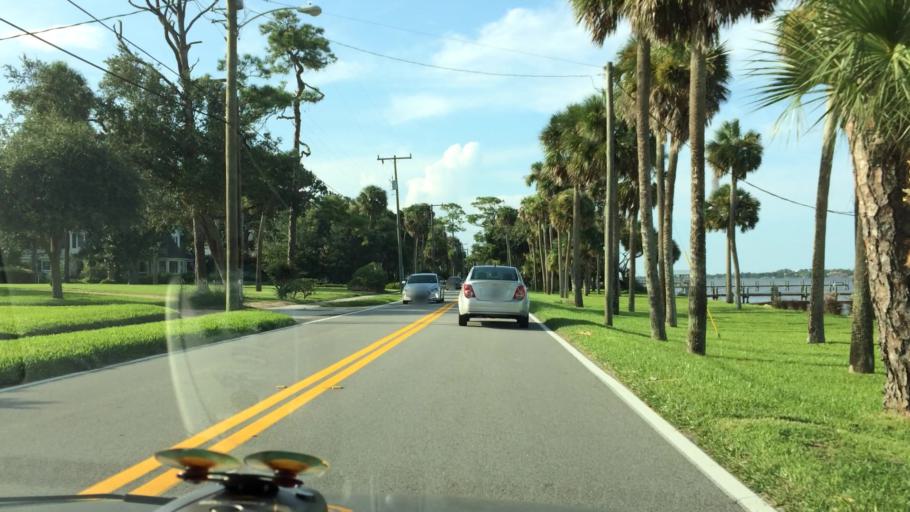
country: US
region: Florida
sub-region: Volusia County
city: Ormond Beach
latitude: 29.2880
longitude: -81.0564
